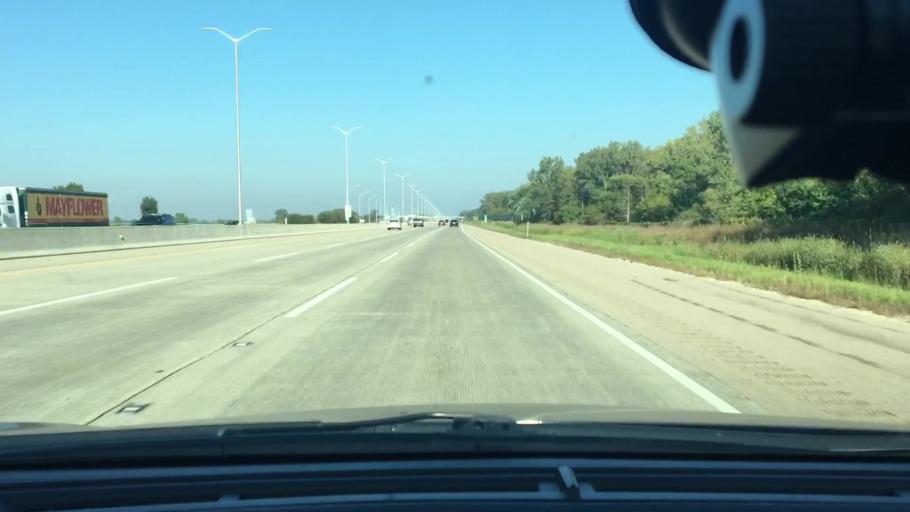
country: US
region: Illinois
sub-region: Kane County
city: Hampshire
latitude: 42.1641
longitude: -88.5787
